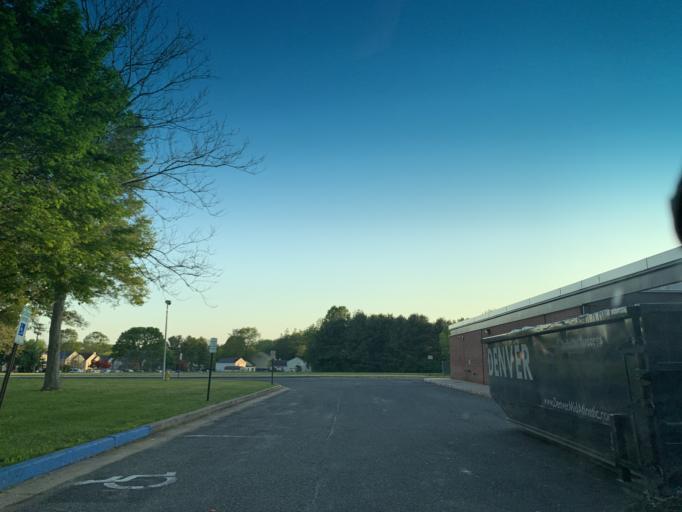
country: US
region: Maryland
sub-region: Harford County
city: Aberdeen
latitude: 39.5034
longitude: -76.1798
